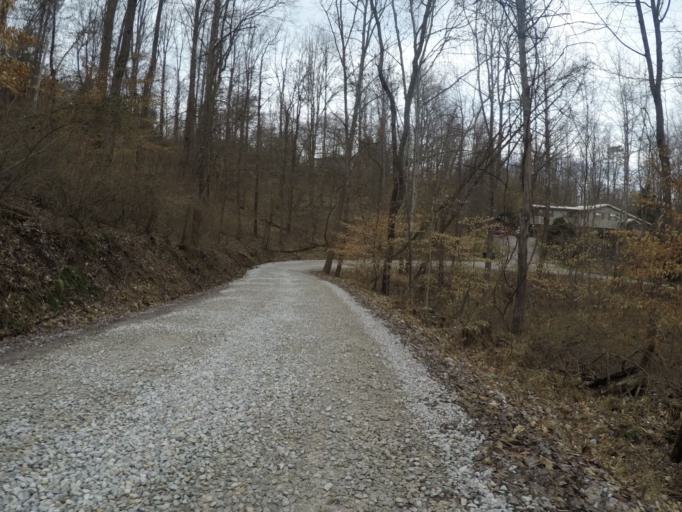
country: US
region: West Virginia
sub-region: Cabell County
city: Pea Ridge
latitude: 38.3891
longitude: -82.3820
